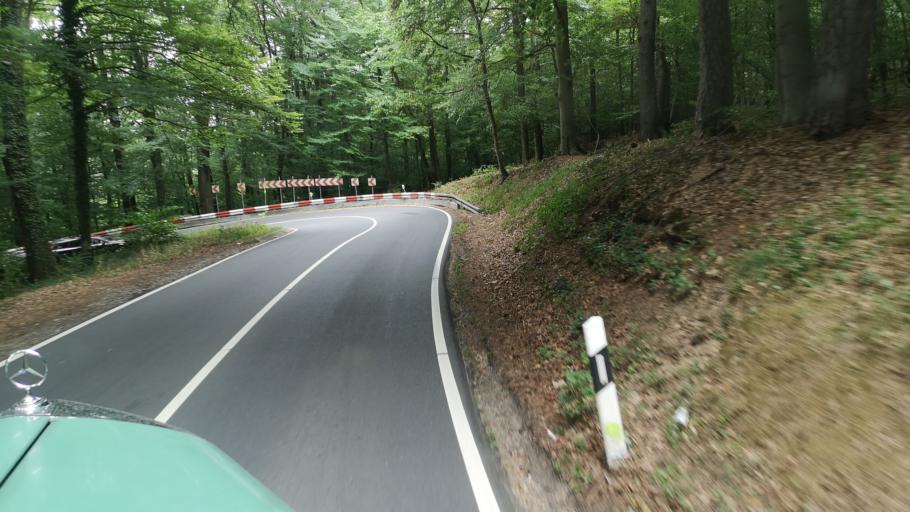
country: DE
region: North Rhine-Westphalia
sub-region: Regierungsbezirk Koln
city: Odenthal
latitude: 51.0551
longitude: 7.1401
